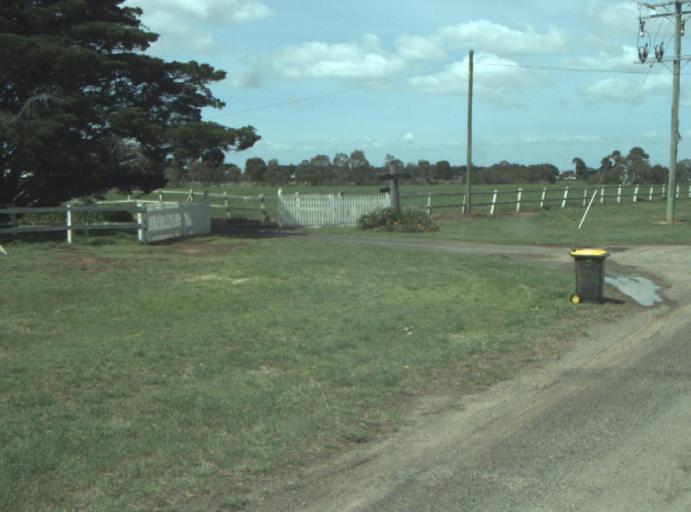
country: AU
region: Victoria
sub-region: Wyndham
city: Little River
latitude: -37.9755
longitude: 144.5105
